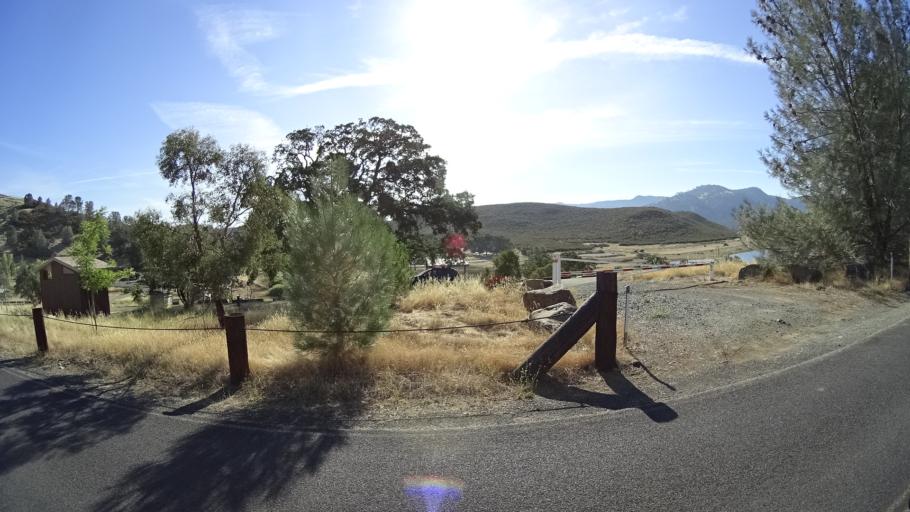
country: US
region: California
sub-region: Calaveras County
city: Valley Springs
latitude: 38.1803
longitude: -120.7943
